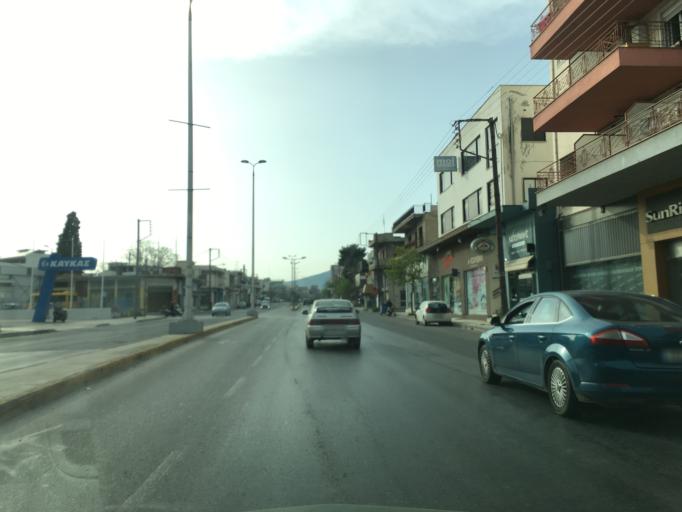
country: GR
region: Thessaly
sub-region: Nomos Magnisias
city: Nea Ionia
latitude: 39.3642
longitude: 22.9285
